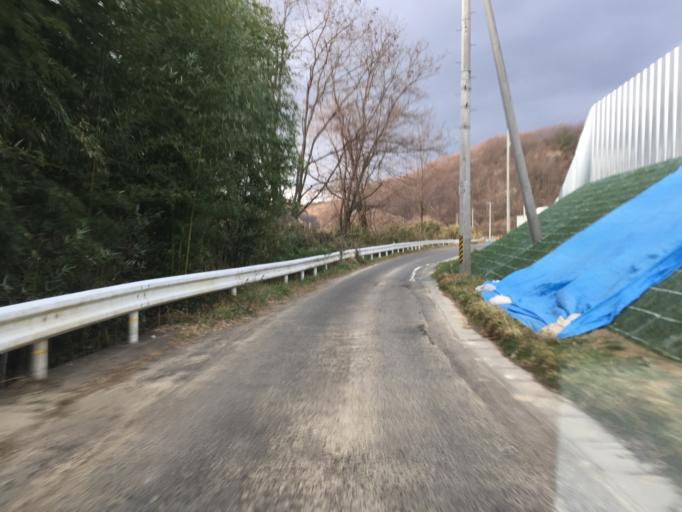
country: JP
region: Fukushima
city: Motomiya
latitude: 37.5265
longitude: 140.4150
